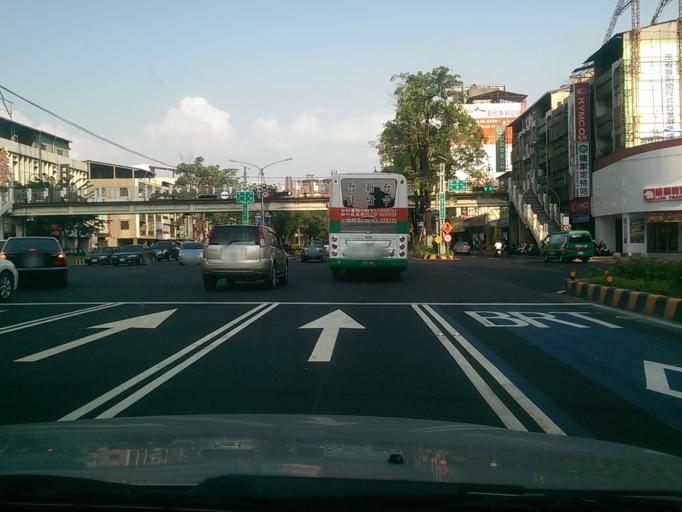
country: TW
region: Taiwan
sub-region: Taichung City
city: Taichung
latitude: 24.1609
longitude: 120.6527
